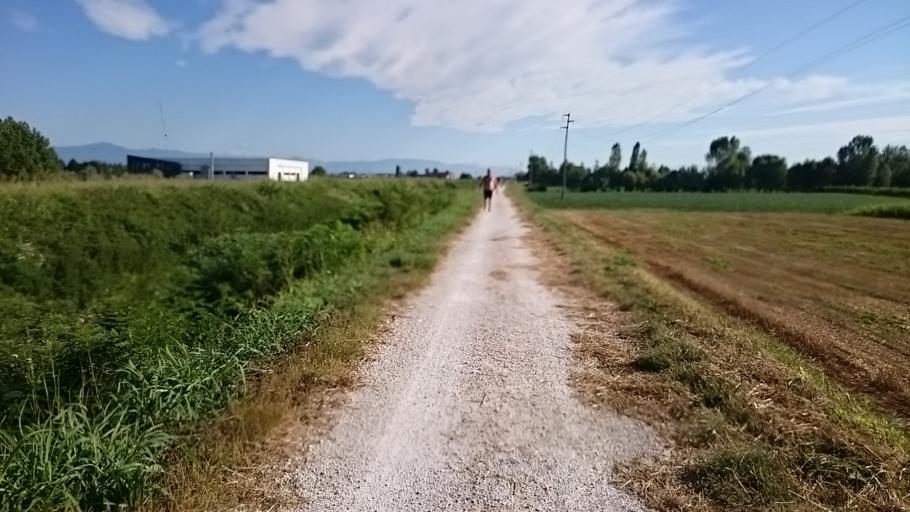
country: IT
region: Veneto
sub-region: Provincia di Padova
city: Borgoricco-San Michele delle Badesse-Sant'Eufemia
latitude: 45.5292
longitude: 11.9221
